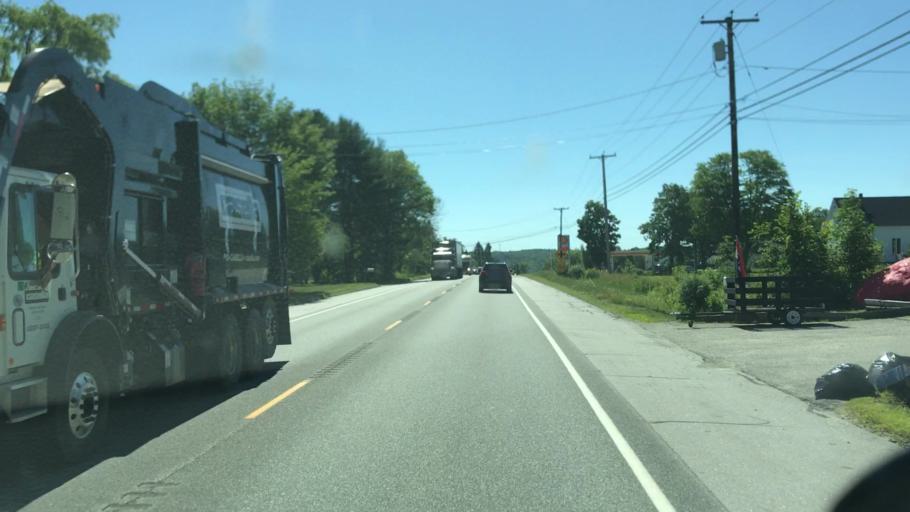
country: US
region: Maine
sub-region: Penobscot County
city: Holden
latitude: 44.7508
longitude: -68.6518
